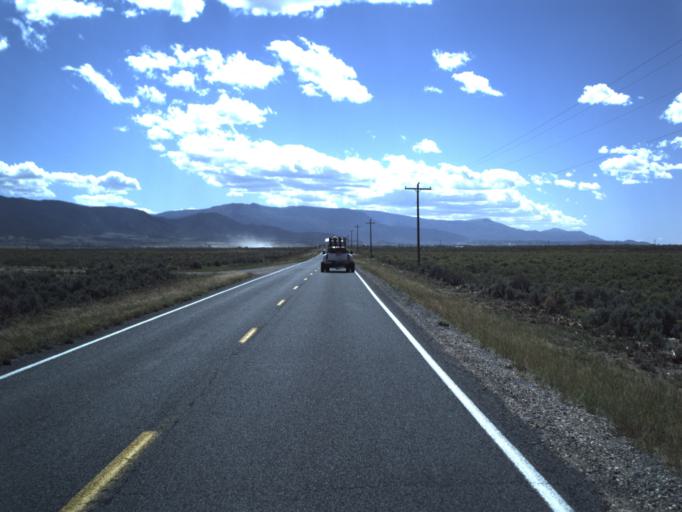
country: US
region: Utah
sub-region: Iron County
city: Enoch
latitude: 37.8289
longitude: -113.0504
